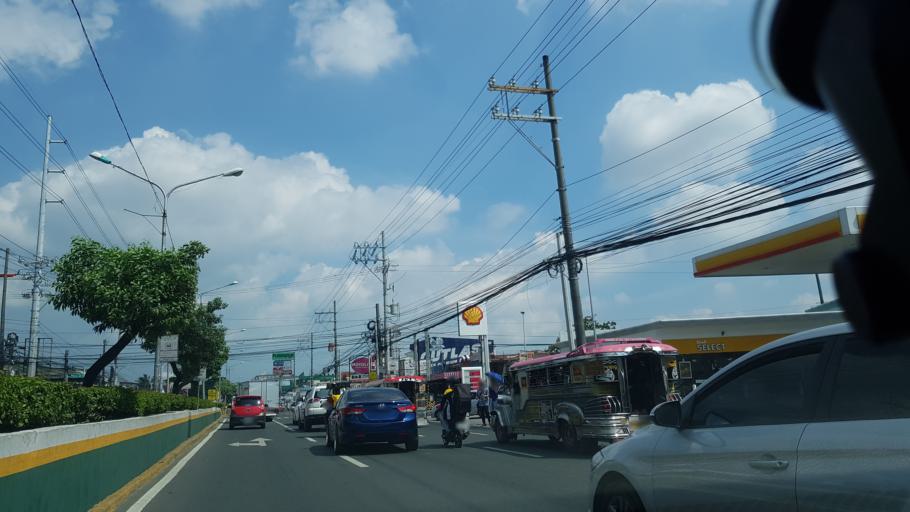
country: PH
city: Sambayanihan People's Village
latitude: 14.4678
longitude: 121.0135
